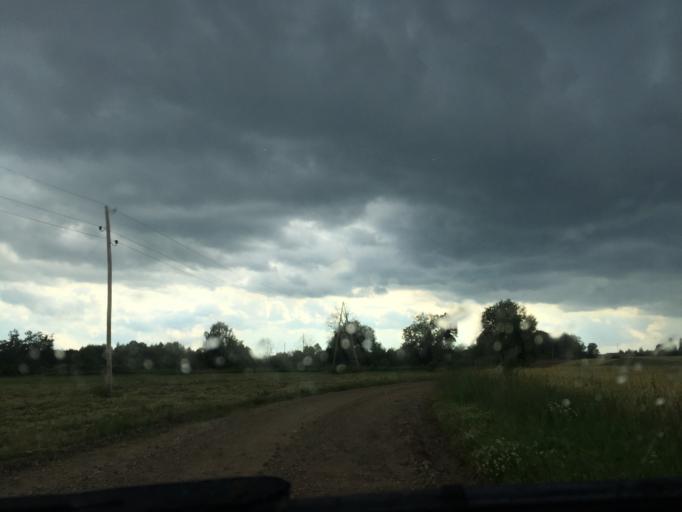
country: LV
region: Dobeles Rajons
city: Dobele
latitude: 56.6156
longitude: 23.3385
